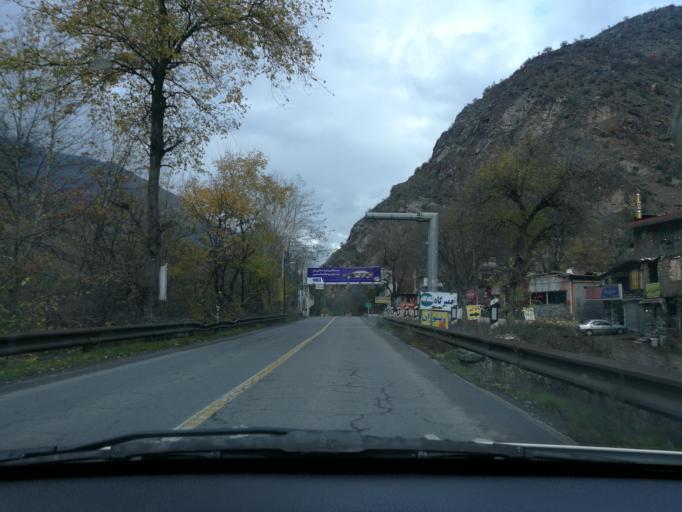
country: IR
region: Mazandaran
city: Chalus
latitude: 36.3382
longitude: 51.2580
